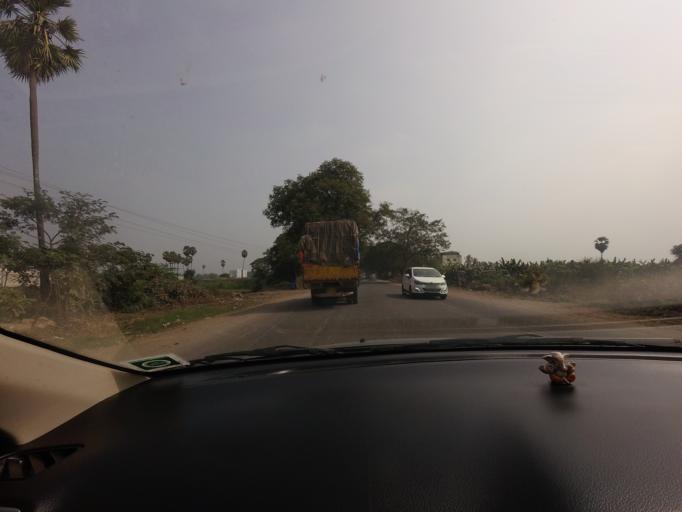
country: IN
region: Andhra Pradesh
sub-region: Krishna
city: Kankipadu
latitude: 16.4411
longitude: 80.7588
